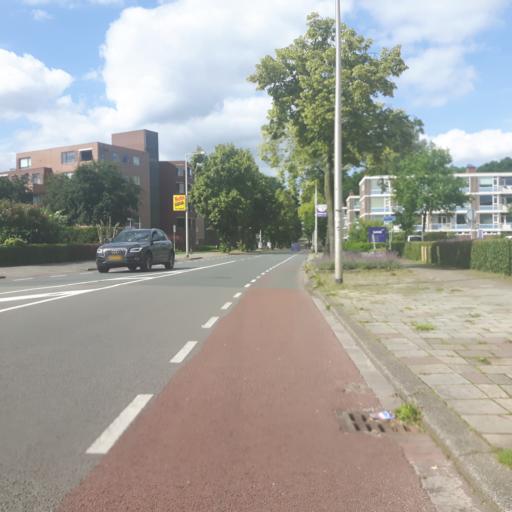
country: NL
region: Overijssel
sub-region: Gemeente Enschede
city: Enschede
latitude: 52.2072
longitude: 6.8807
